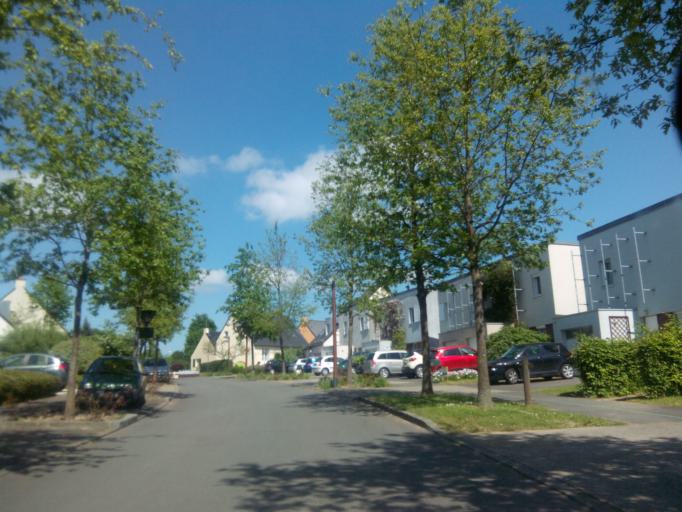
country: FR
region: Brittany
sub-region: Departement d'Ille-et-Vilaine
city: Fouillard
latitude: 48.1561
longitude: -1.5863
